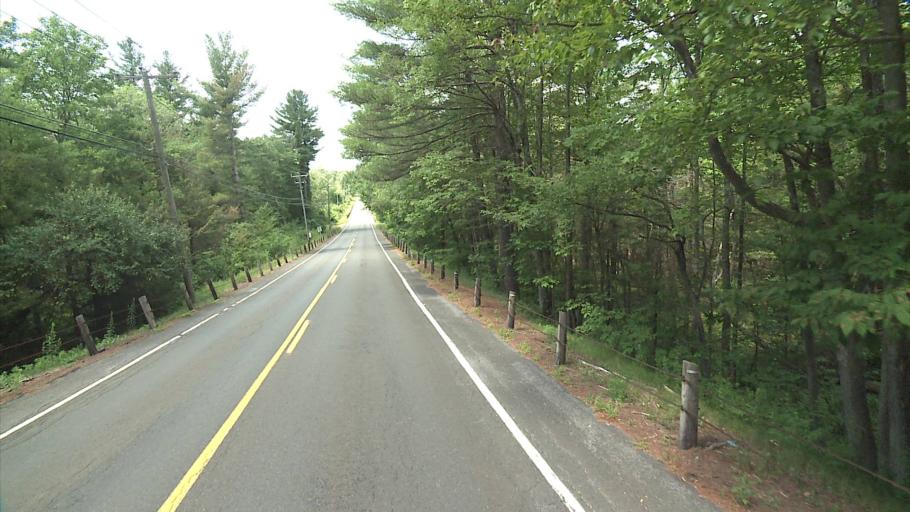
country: US
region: Connecticut
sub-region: Litchfield County
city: Winsted
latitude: 41.9846
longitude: -73.1146
